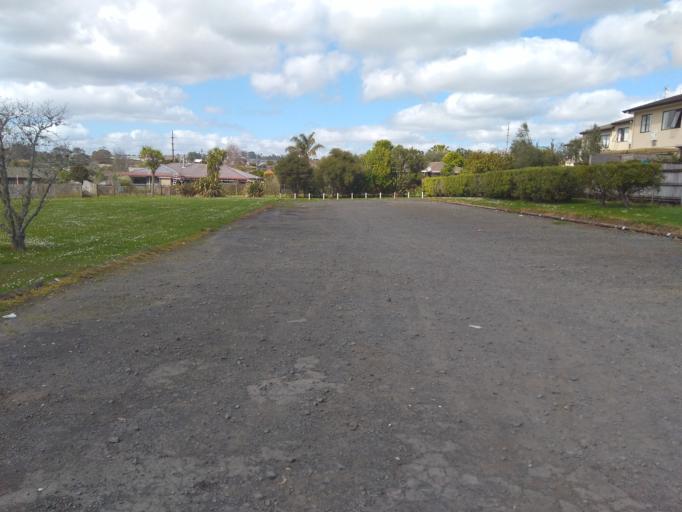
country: NZ
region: Auckland
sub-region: Auckland
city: Rothesay Bay
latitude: -36.7370
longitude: 174.6937
